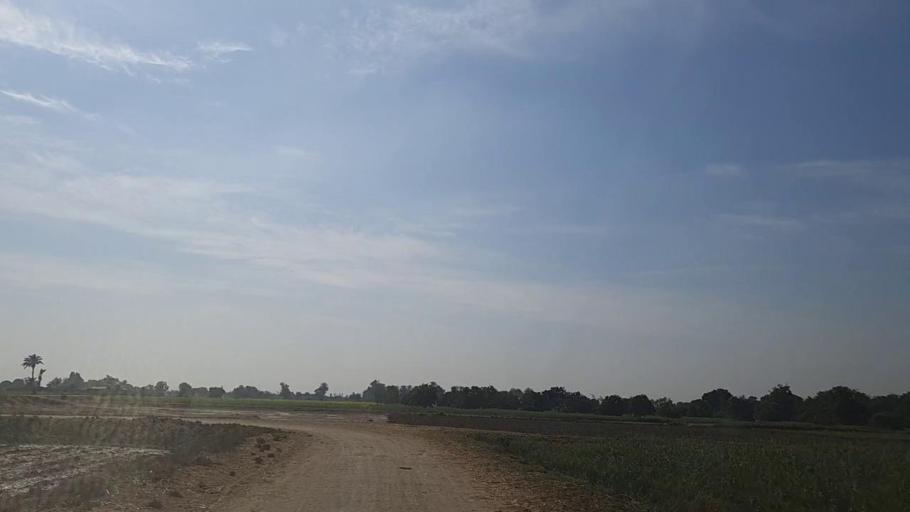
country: PK
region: Sindh
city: Mirpur Khas
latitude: 25.4728
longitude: 68.9639
